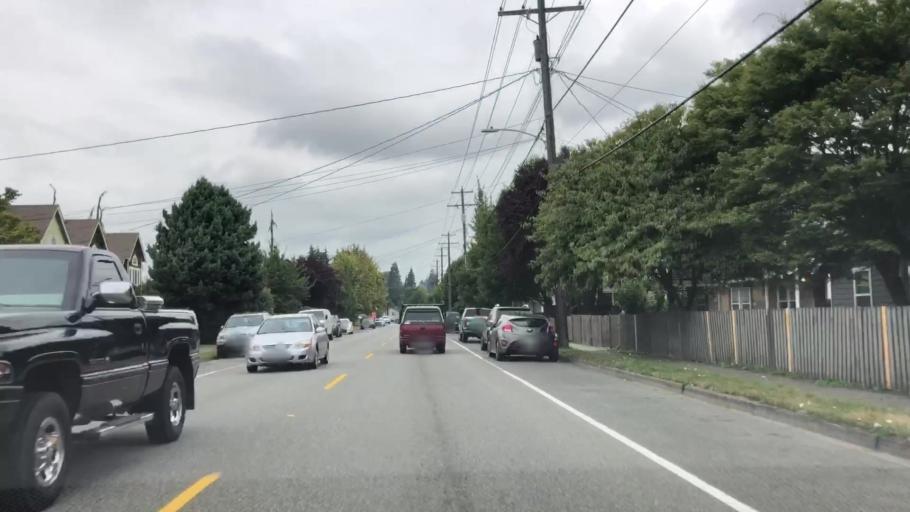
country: US
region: Washington
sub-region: Snohomish County
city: Snohomish
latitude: 47.9159
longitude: -122.0860
